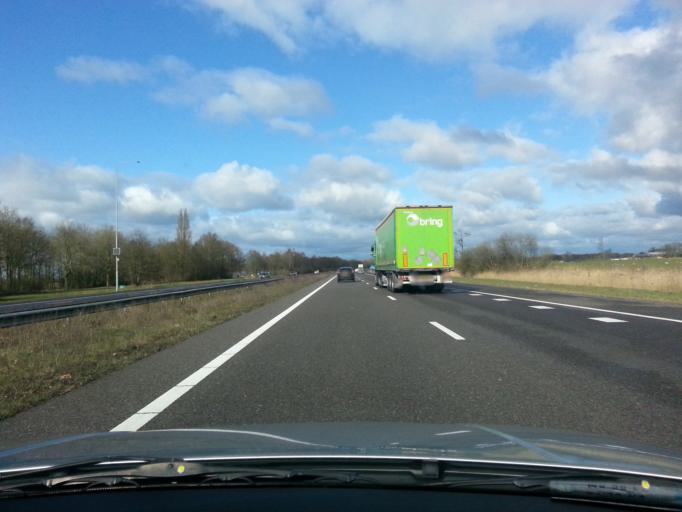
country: NL
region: Gelderland
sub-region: Gemeente Ermelo
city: Horst
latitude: 52.2995
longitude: 5.5544
